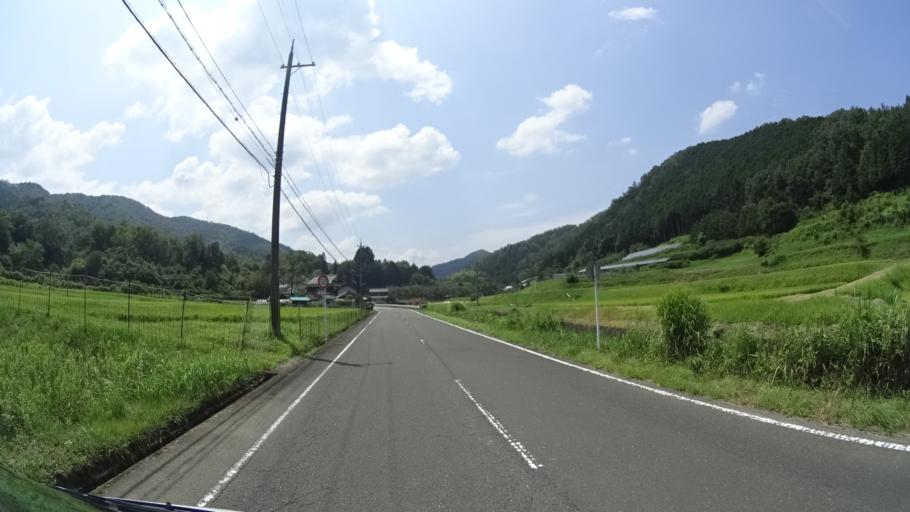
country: JP
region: Kyoto
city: Ayabe
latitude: 35.2169
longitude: 135.2133
